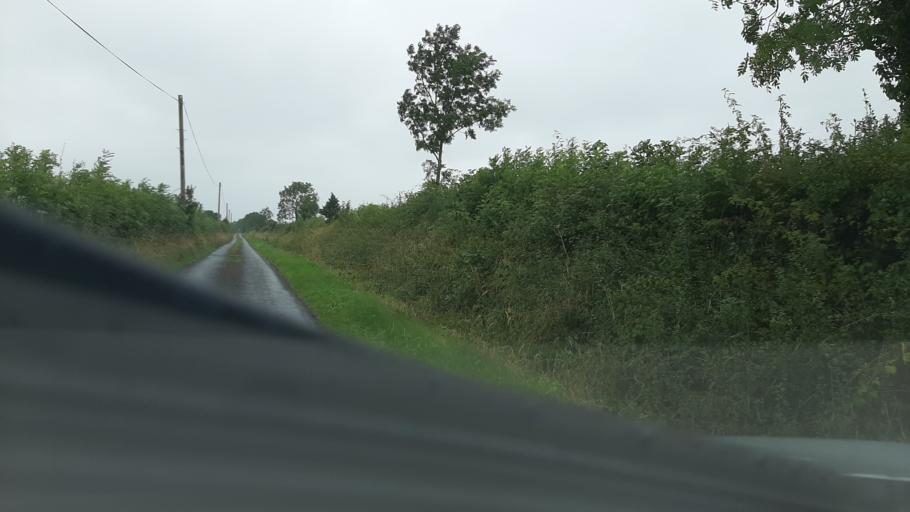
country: IE
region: Leinster
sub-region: Kildare
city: Rathangan
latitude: 53.1983
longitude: -7.0454
